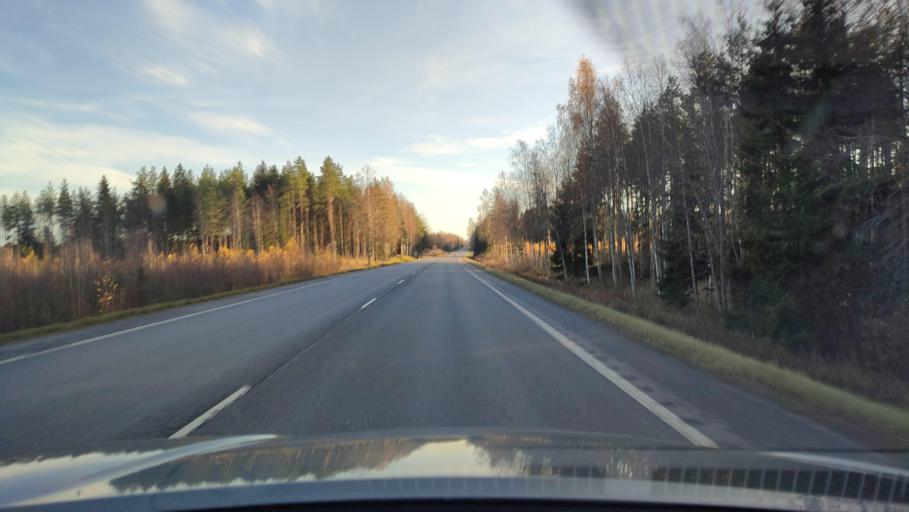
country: FI
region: Ostrobothnia
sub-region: Vaasa
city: Ristinummi
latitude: 63.0111
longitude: 21.7617
